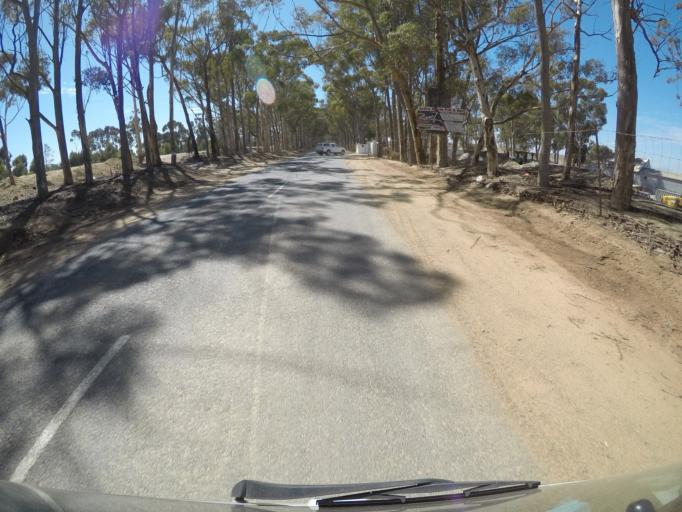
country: ZA
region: Western Cape
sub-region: City of Cape Town
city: Sunset Beach
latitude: -33.7634
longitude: 18.5515
